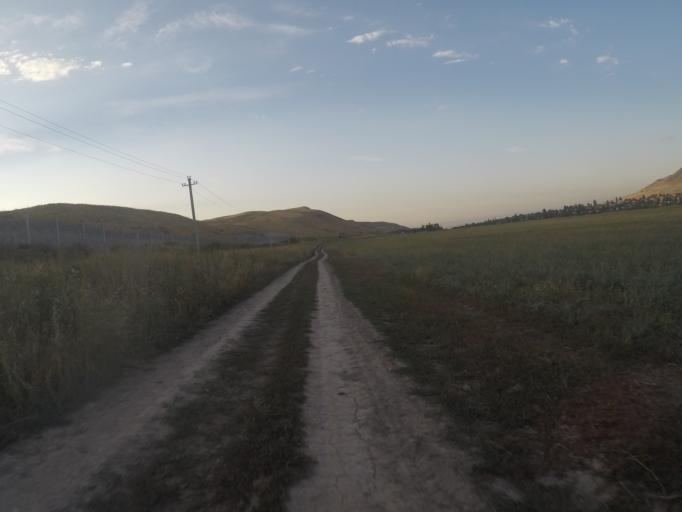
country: KG
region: Chuy
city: Bishkek
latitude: 42.7574
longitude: 74.6361
